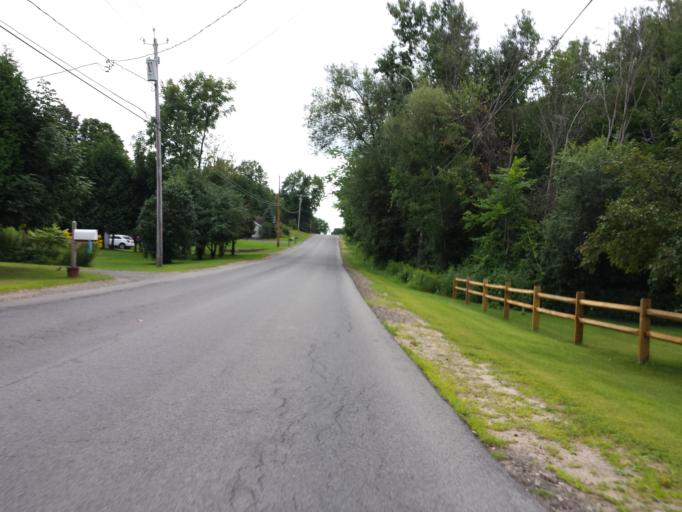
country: US
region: New York
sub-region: St. Lawrence County
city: Potsdam
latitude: 44.7006
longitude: -75.0118
